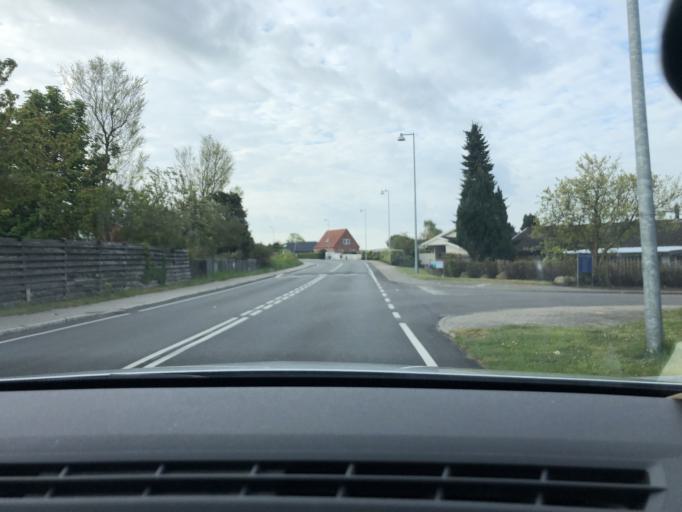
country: DK
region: Zealand
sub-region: Faxe Kommune
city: Ronnede
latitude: 55.2516
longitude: 12.0341
